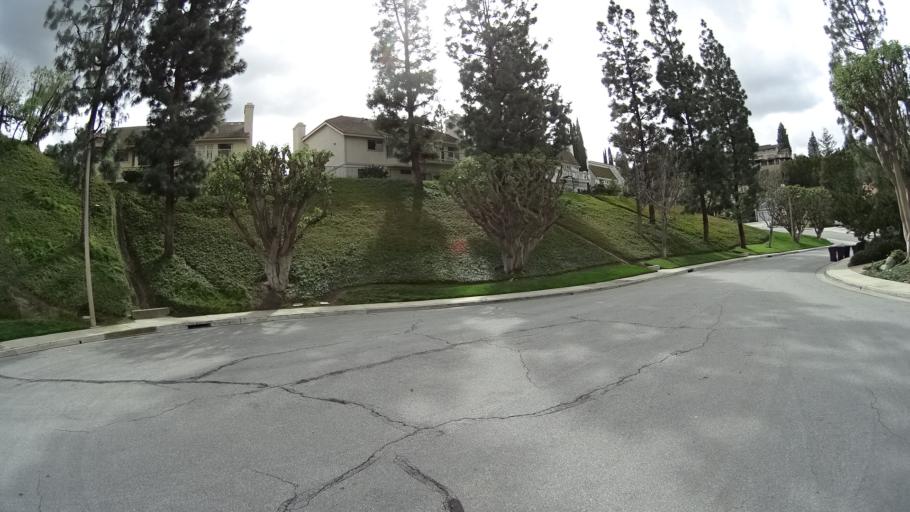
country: US
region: California
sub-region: Orange County
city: Villa Park
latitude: 33.8415
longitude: -117.7847
